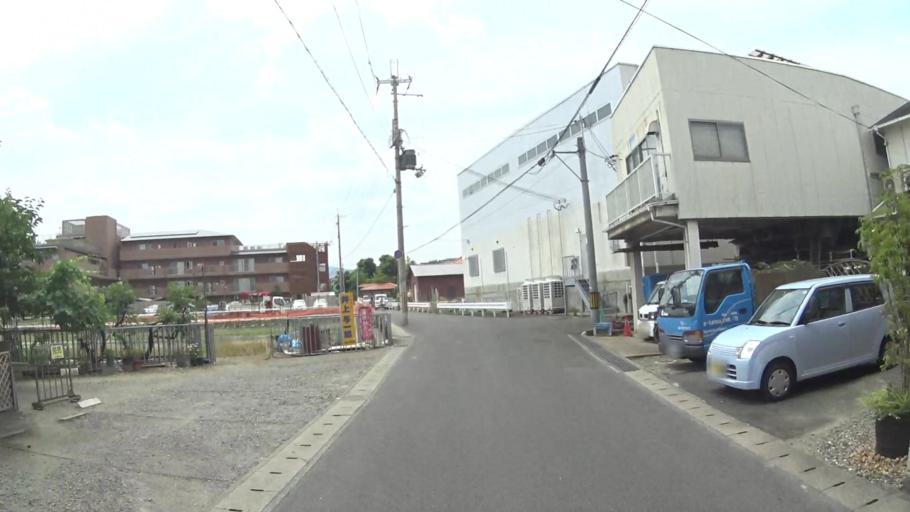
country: JP
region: Kyoto
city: Kyoto
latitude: 35.0179
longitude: 135.7119
